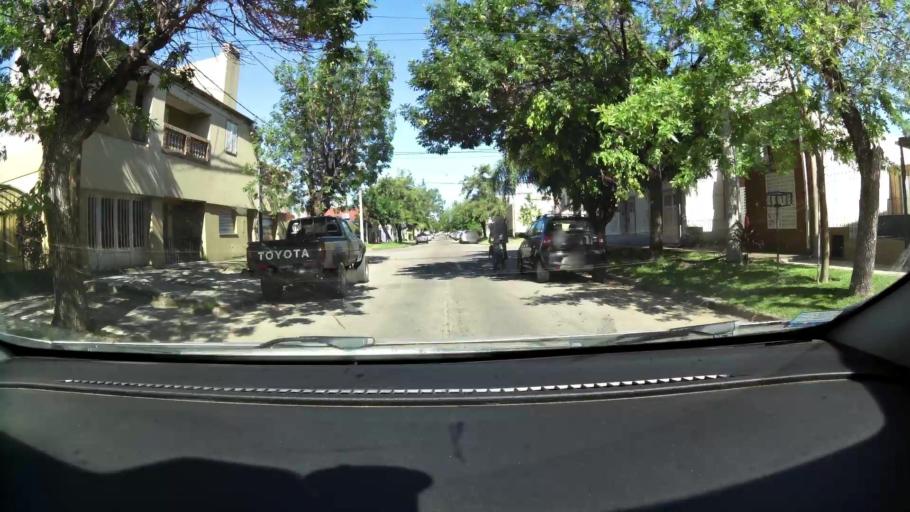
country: AR
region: Santa Fe
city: Santa Fe de la Vera Cruz
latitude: -31.6270
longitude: -60.6930
